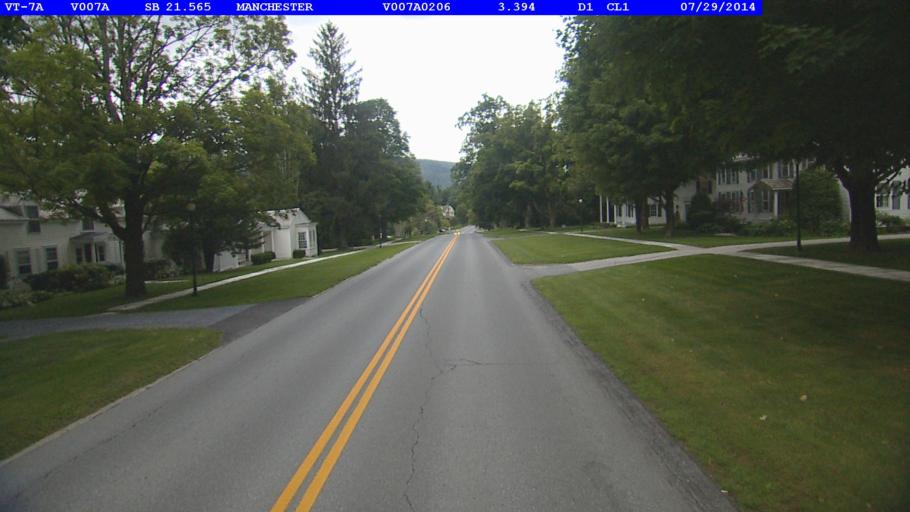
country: US
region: Vermont
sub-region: Bennington County
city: Manchester Center
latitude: 43.1595
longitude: -73.0723
